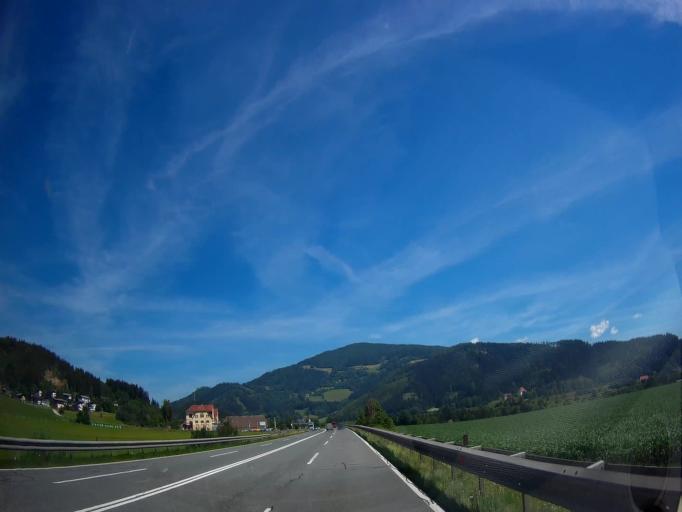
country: AT
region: Carinthia
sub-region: Politischer Bezirk Sankt Veit an der Glan
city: Althofen
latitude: 46.8719
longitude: 14.4495
